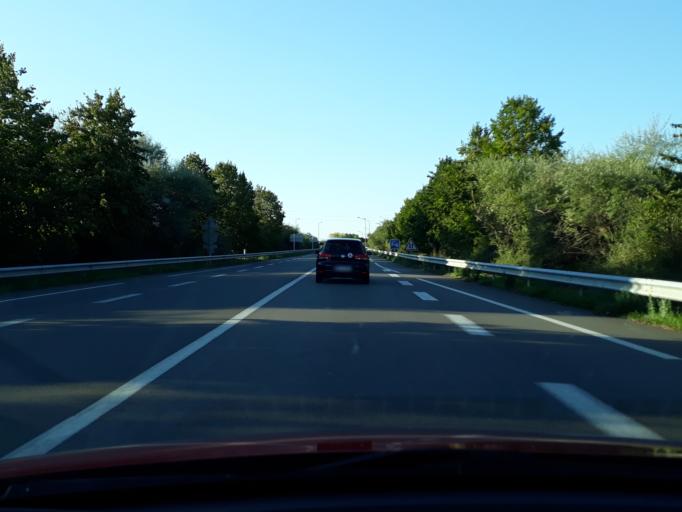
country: FR
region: Rhone-Alpes
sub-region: Departement du Rhone
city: Corbas
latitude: 45.6850
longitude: 4.8855
